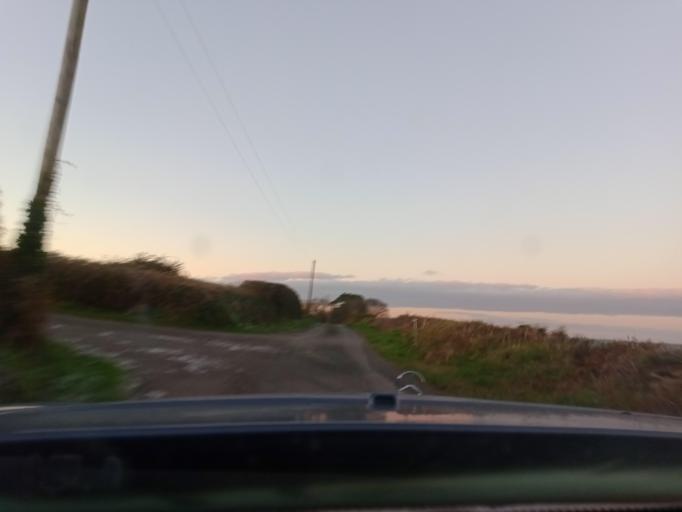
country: IE
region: Leinster
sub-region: Kilkenny
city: Graiguenamanagh
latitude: 52.5798
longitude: -6.9607
